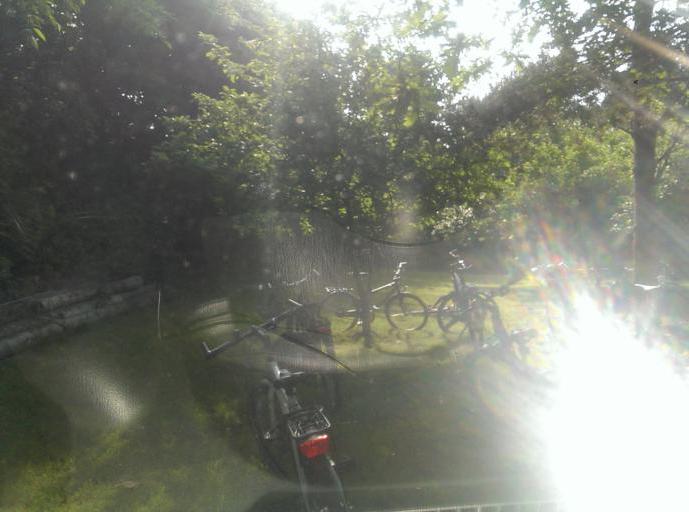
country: DK
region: South Denmark
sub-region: Esbjerg Kommune
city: Bramming
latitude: 55.4282
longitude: 8.6606
